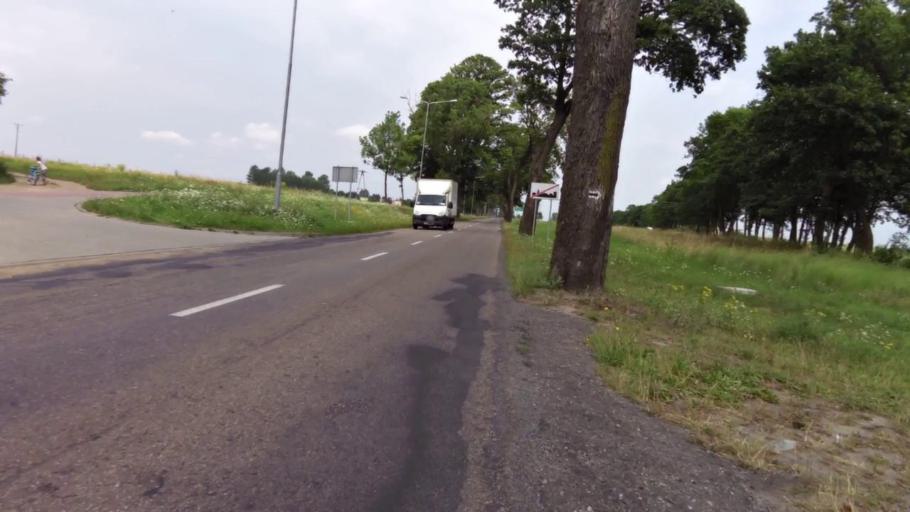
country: PL
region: West Pomeranian Voivodeship
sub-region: Powiat drawski
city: Drawsko Pomorskie
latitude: 53.5443
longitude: 15.8164
